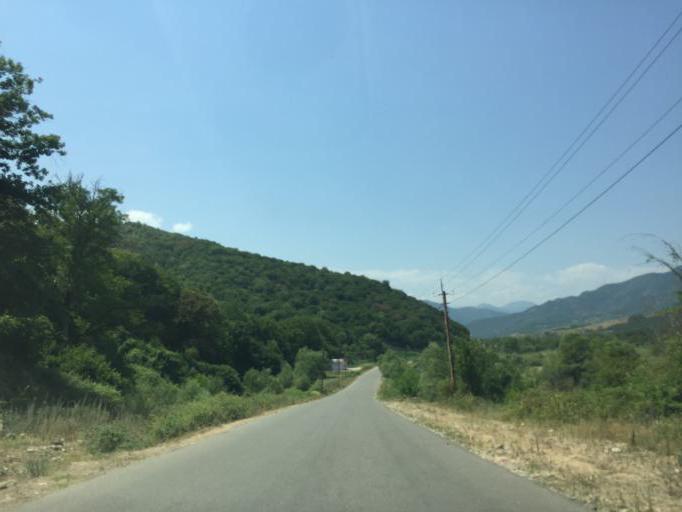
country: AZ
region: Tartar Rayon
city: Martakert
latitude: 40.1340
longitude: 46.4830
